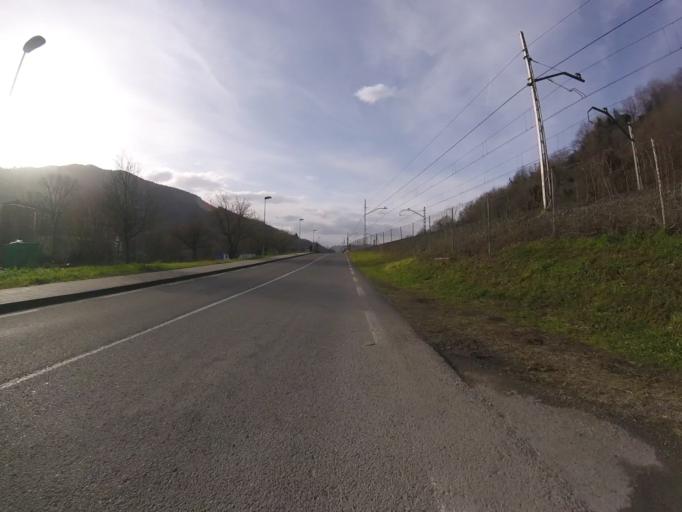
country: ES
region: Basque Country
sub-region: Provincia de Guipuzcoa
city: Villabona
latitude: 43.1842
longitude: -2.0555
